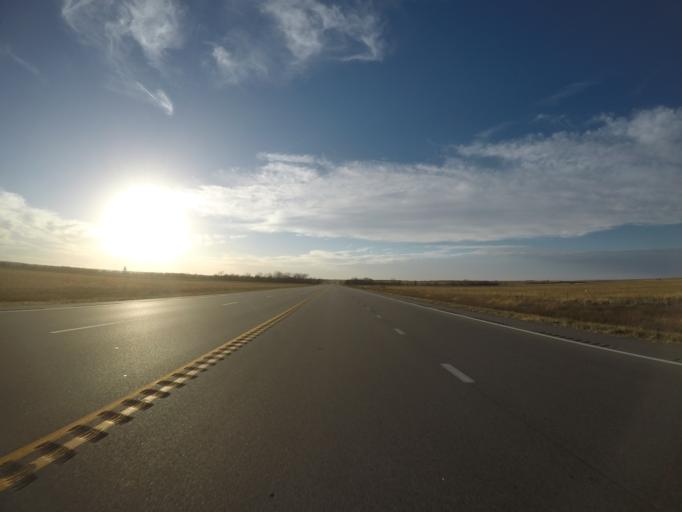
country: US
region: Kansas
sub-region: Chase County
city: Cottonwood Falls
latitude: 38.4056
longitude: -96.4167
